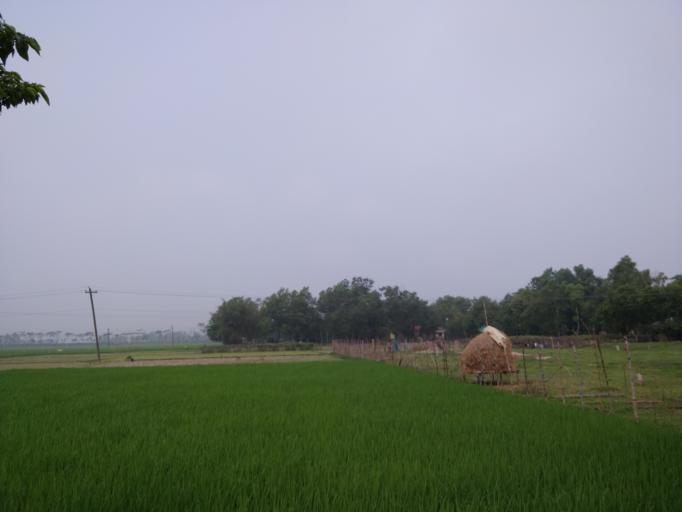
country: BD
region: Sylhet
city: Habiganj
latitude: 24.1676
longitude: 91.3544
